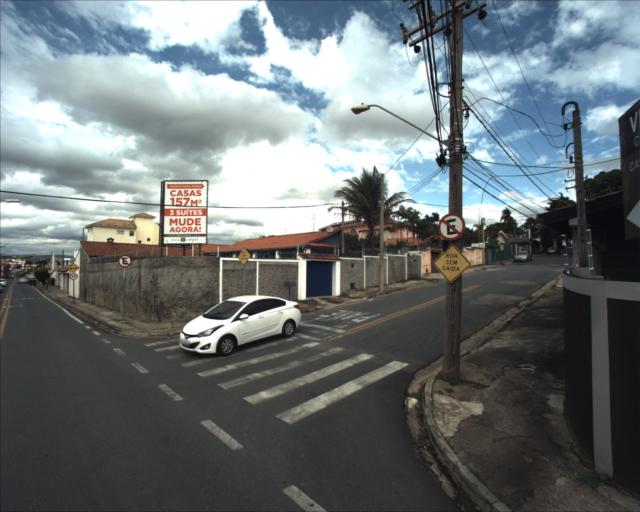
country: BR
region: Sao Paulo
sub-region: Sorocaba
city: Sorocaba
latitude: -23.5209
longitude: -47.4812
